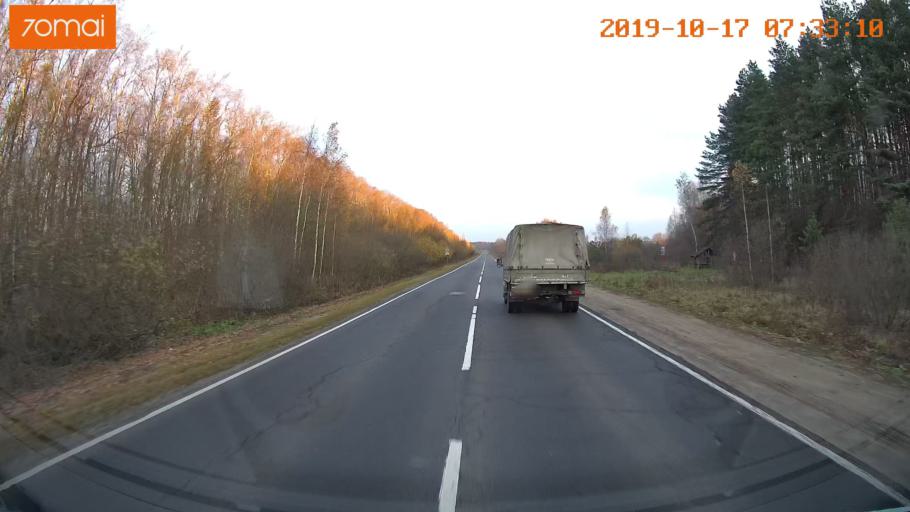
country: RU
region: Ivanovo
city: Gavrilov Posad
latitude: 56.4029
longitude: 39.9606
